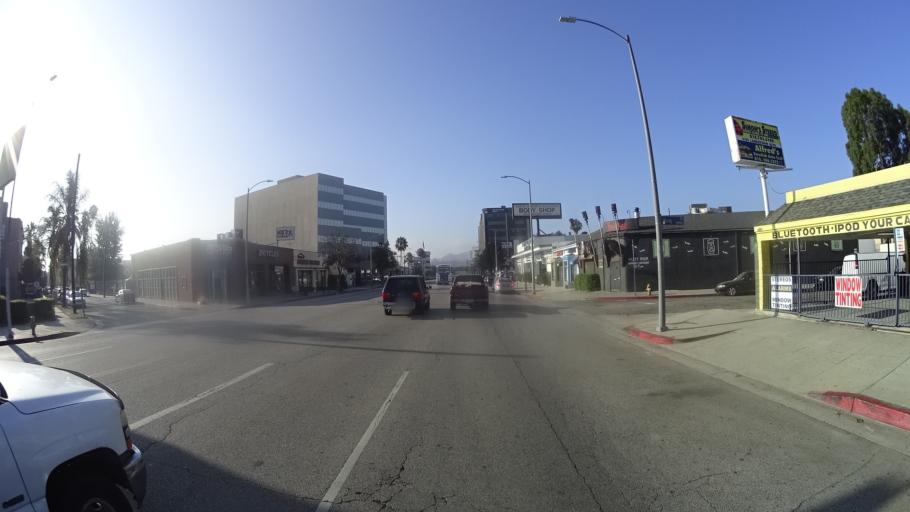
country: US
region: California
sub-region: Los Angeles County
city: North Hollywood
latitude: 34.1559
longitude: -118.3693
